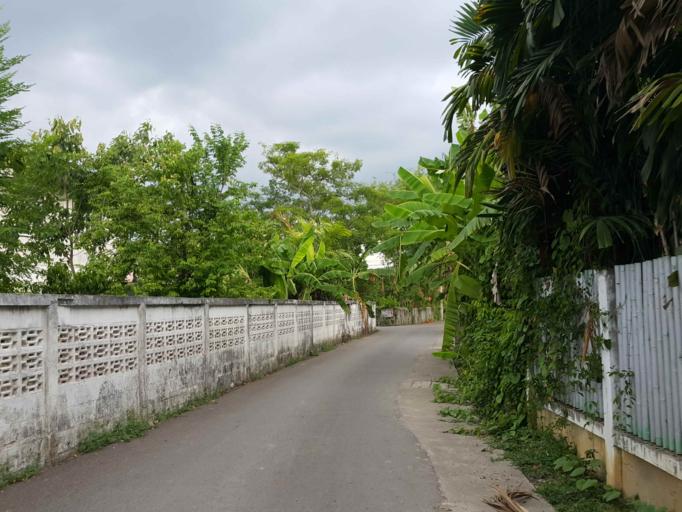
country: TH
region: Chiang Mai
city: Saraphi
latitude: 18.7114
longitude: 99.0354
